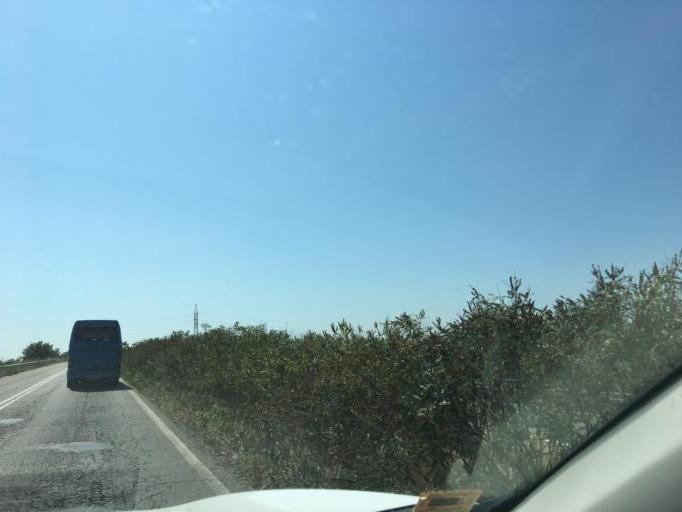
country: BG
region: Burgas
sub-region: Obshtina Kameno
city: Kameno
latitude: 42.5950
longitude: 27.3925
